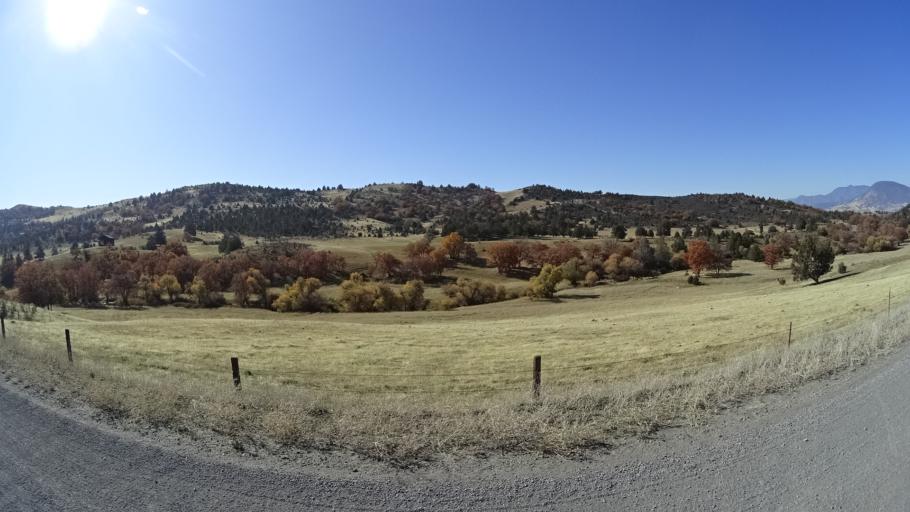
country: US
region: California
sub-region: Siskiyou County
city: Montague
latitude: 41.7976
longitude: -122.3666
